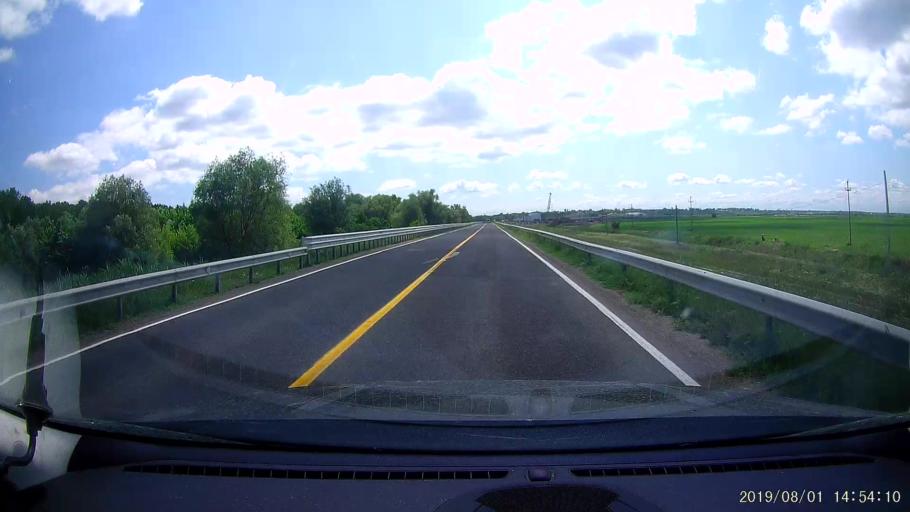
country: RO
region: Braila
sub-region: Municipiul Braila
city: Braila
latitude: 45.3220
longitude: 27.9932
